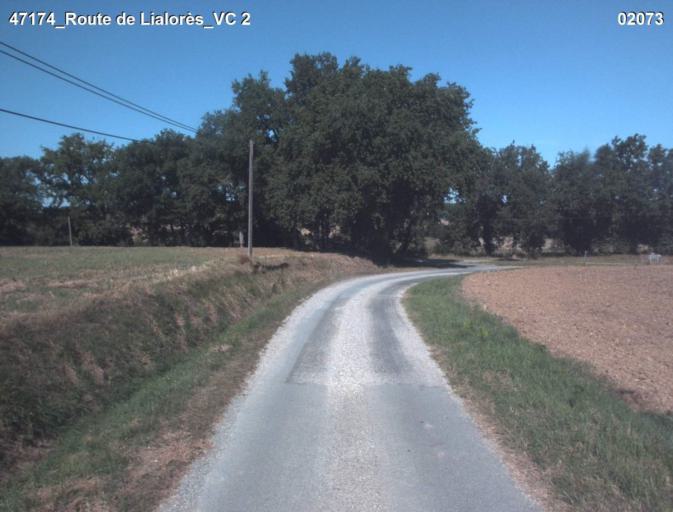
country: FR
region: Midi-Pyrenees
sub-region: Departement du Gers
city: Condom
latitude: 44.0220
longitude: 0.3695
